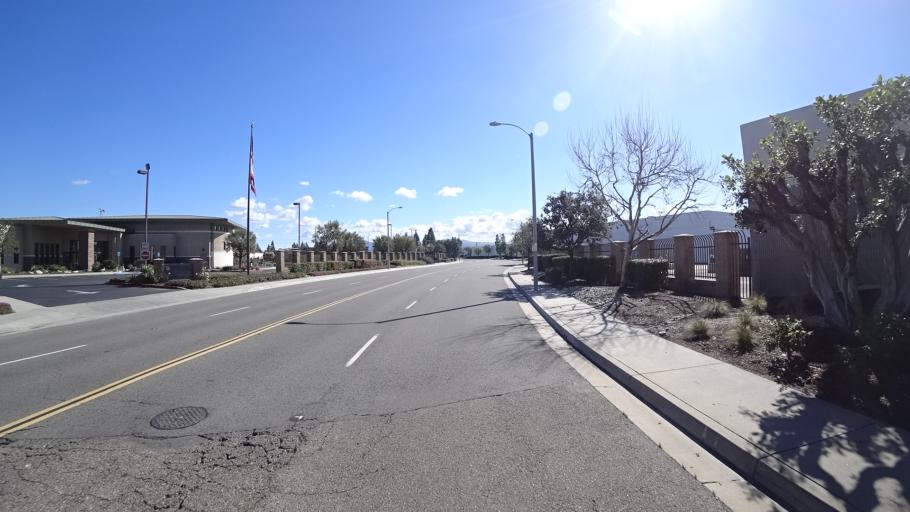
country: US
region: California
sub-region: Orange County
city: Yorba Linda
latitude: 33.8627
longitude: -117.8285
